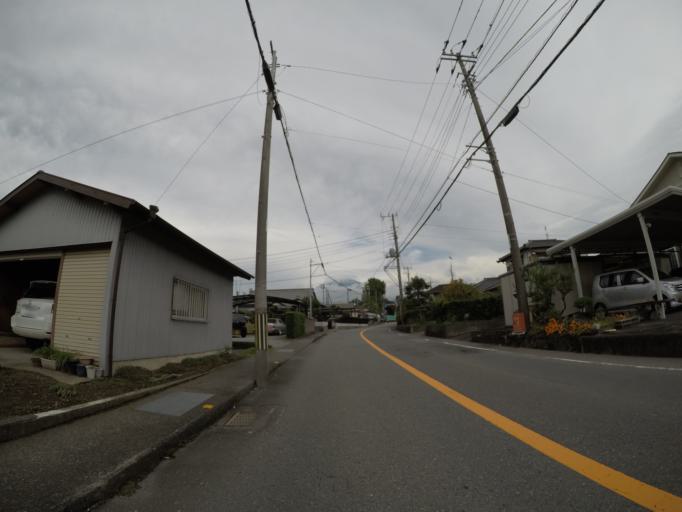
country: JP
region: Shizuoka
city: Fuji
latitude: 35.1935
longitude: 138.6524
